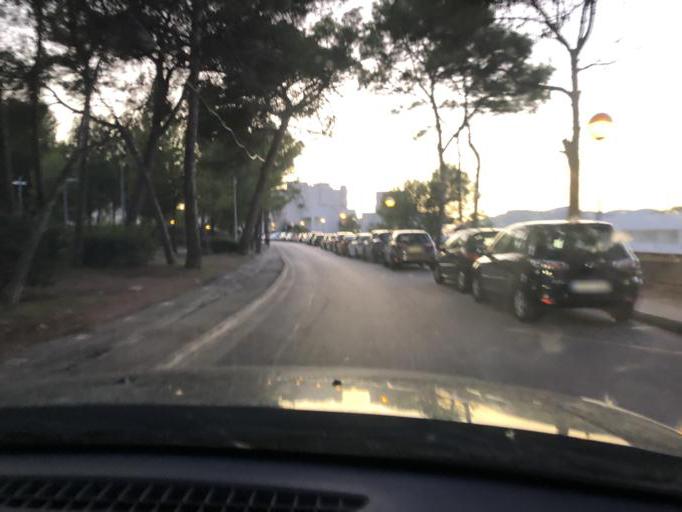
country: ES
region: Balearic Islands
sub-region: Illes Balears
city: Santa Ponsa
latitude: 39.5223
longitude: 2.4704
